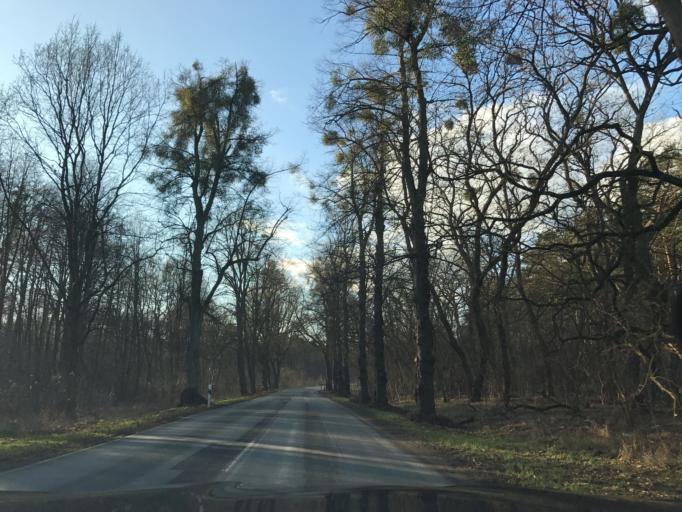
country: DE
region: Saxony-Anhalt
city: Mockern
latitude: 52.1553
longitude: 11.9776
